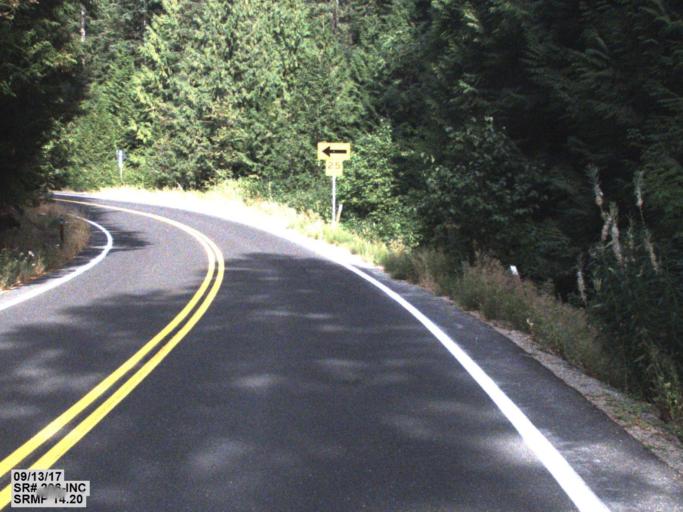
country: US
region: Washington
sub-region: Spokane County
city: Otis Orchards-East Farms
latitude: 47.8763
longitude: -117.1493
